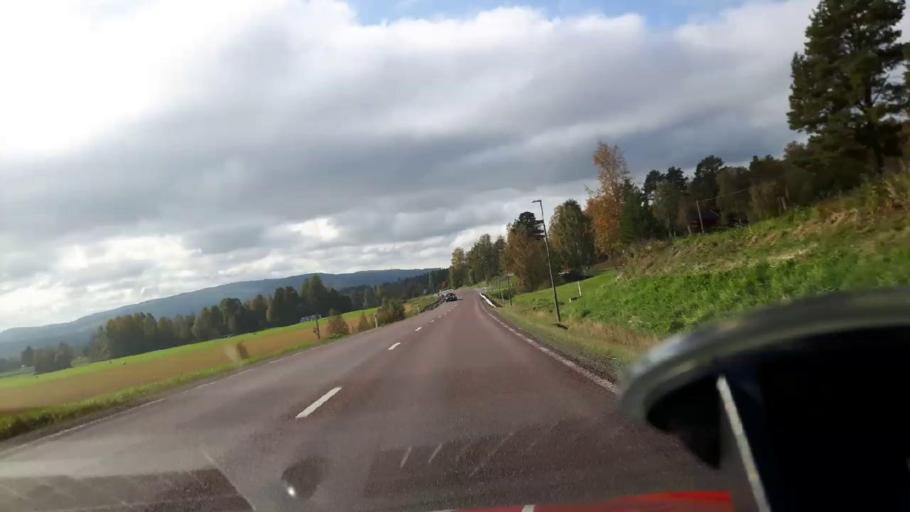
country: SE
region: Gaevleborg
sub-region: Ljusdals Kommun
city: Jaervsoe
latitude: 61.6970
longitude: 16.1599
